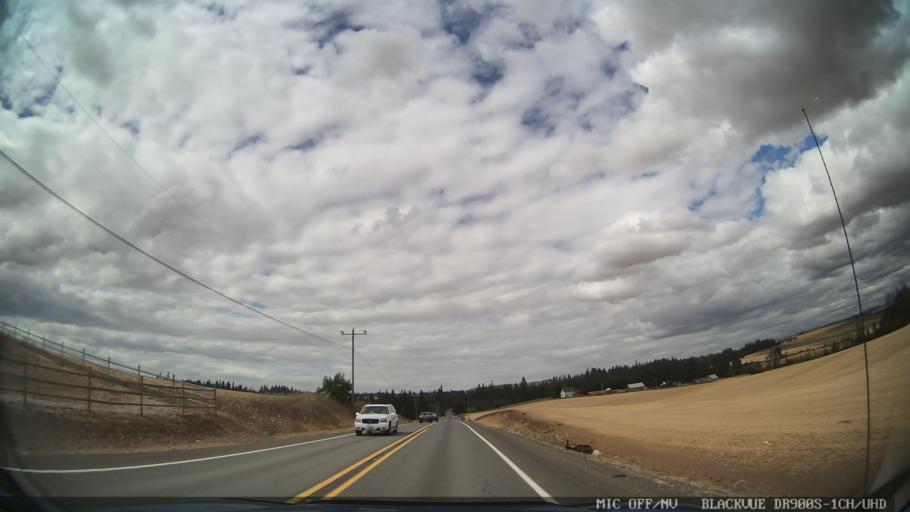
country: US
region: Oregon
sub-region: Marion County
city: Sublimity
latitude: 44.8428
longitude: -122.7945
